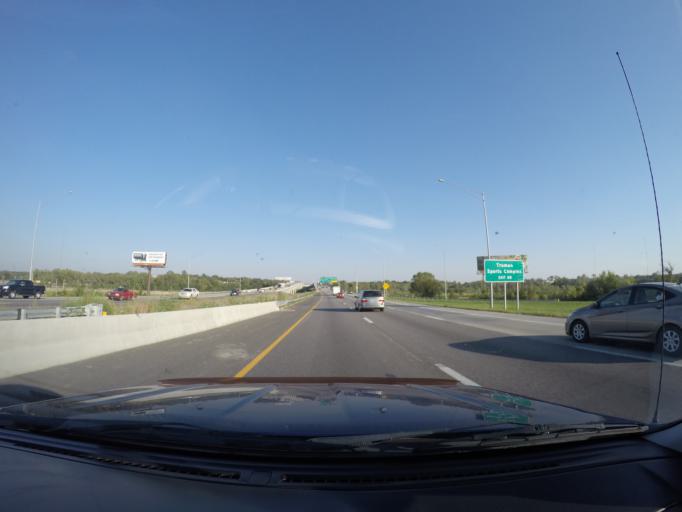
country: US
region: Missouri
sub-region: Jackson County
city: Kansas City
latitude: 39.0682
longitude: -94.5100
